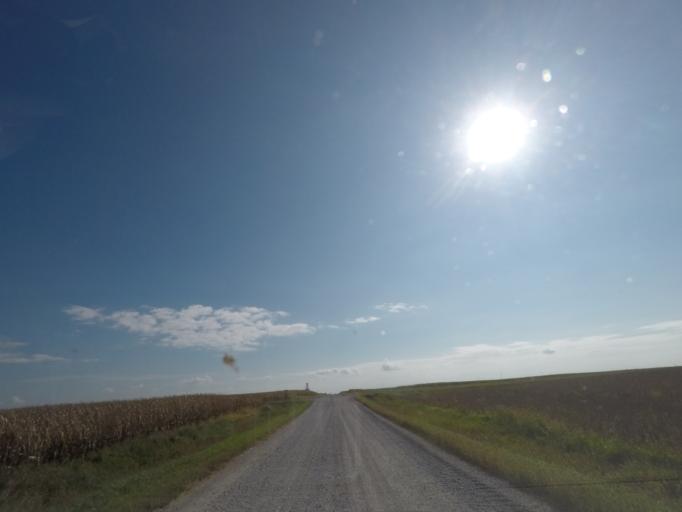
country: US
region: Iowa
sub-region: Story County
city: Nevada
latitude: 42.0490
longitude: -93.4261
